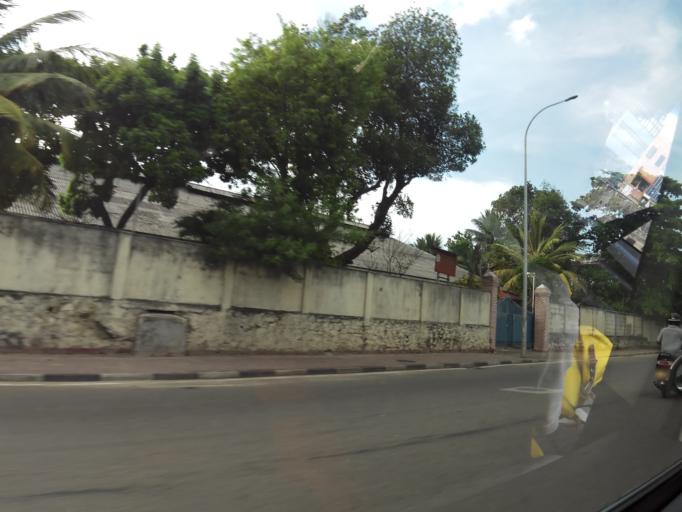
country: LK
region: Western
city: Kolonnawa
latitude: 6.9343
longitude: 79.8782
